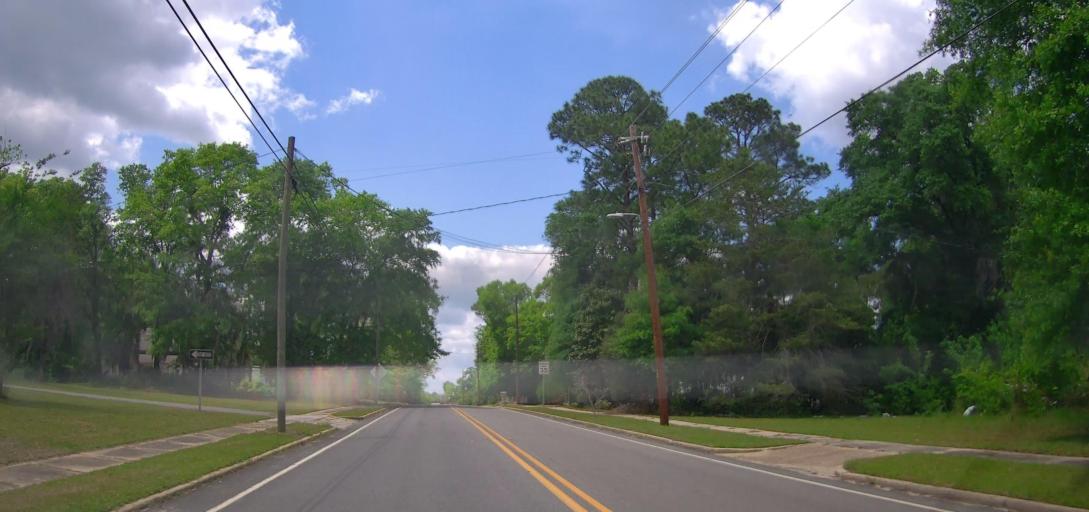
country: US
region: Georgia
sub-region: Treutlen County
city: Soperton
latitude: 32.3753
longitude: -82.5862
